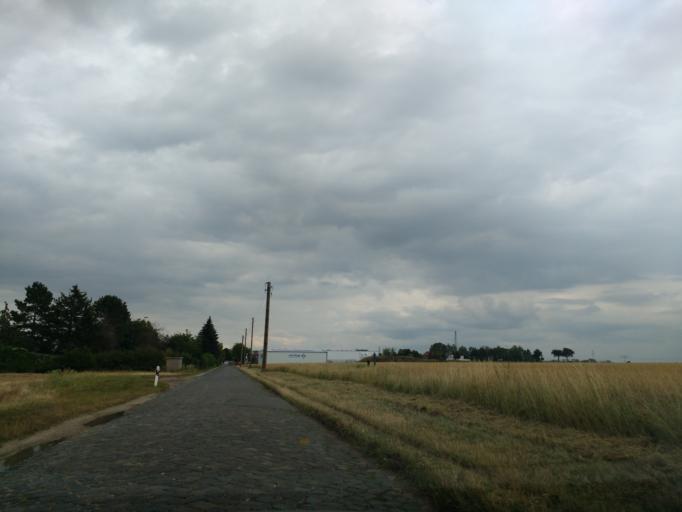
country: DE
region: Saxony-Anhalt
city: Dolbau
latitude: 51.4576
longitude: 12.0590
